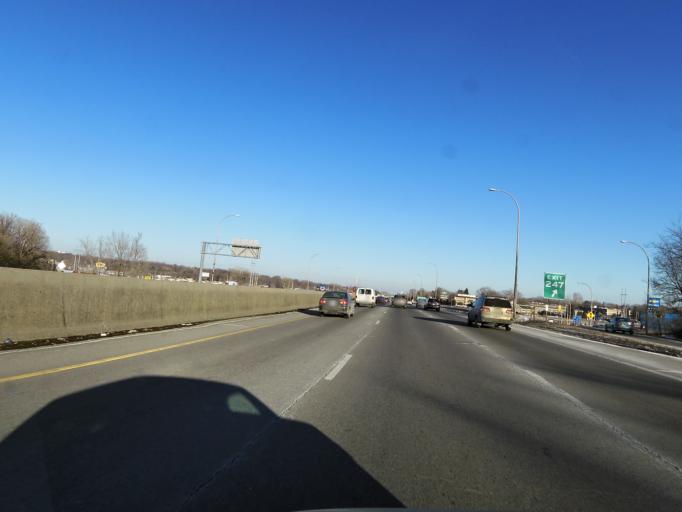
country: US
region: Minnesota
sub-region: Ramsey County
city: Maplewood
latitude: 44.9483
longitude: -92.9894
